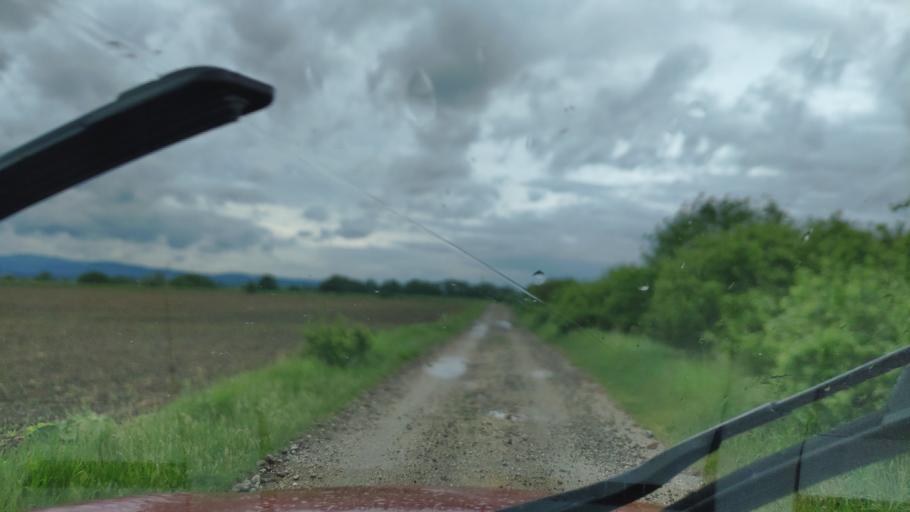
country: SK
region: Kosicky
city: Moldava nad Bodvou
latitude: 48.5536
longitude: 21.1153
